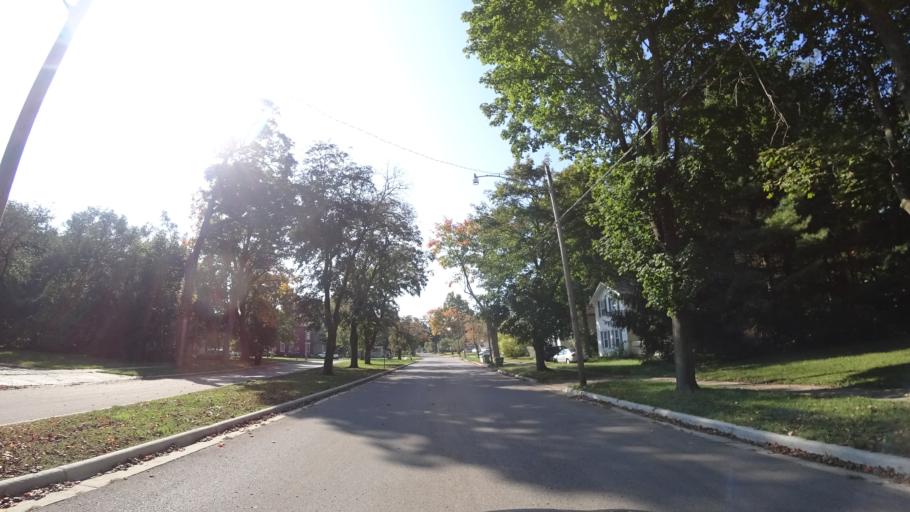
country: US
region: Michigan
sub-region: Saint Joseph County
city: Three Rivers
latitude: 41.9409
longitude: -85.6371
